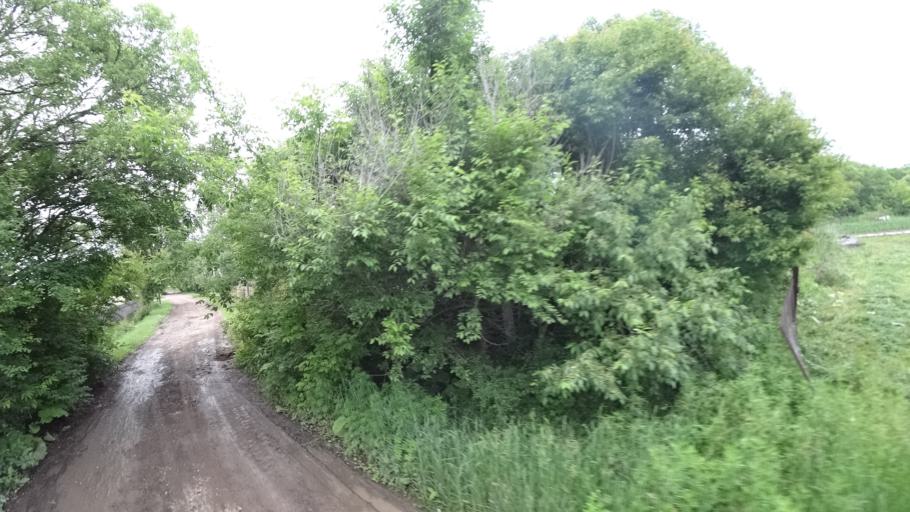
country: RU
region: Primorskiy
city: Novosysoyevka
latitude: 44.2450
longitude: 133.3739
